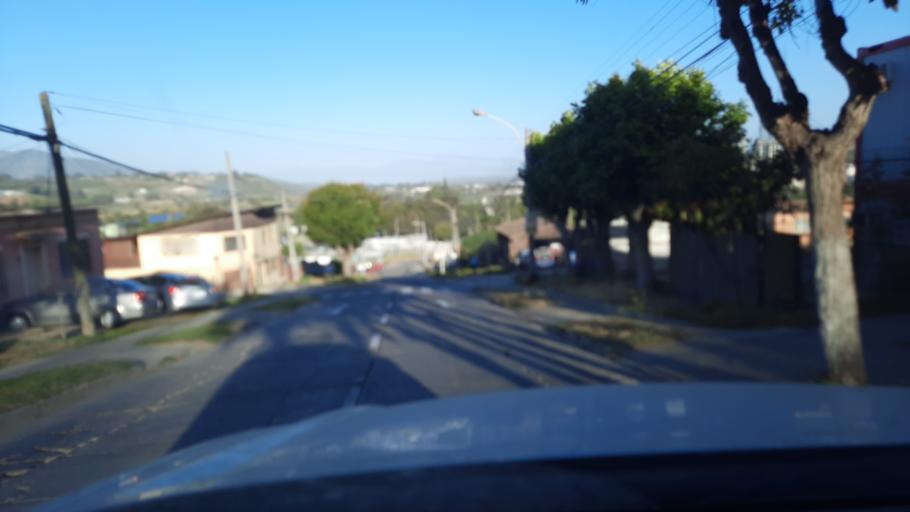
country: CL
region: Valparaiso
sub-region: Provincia de Valparaiso
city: Vina del Mar
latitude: -32.9238
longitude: -71.5081
